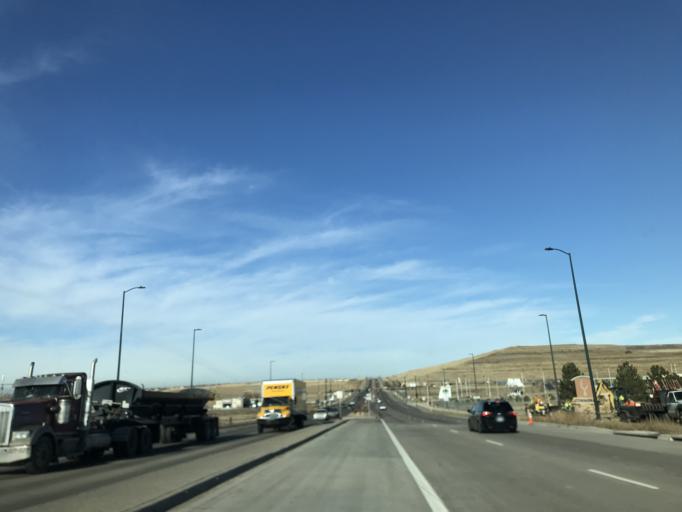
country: US
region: Colorado
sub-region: Adams County
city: Aurora
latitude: 39.8412
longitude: -104.7720
